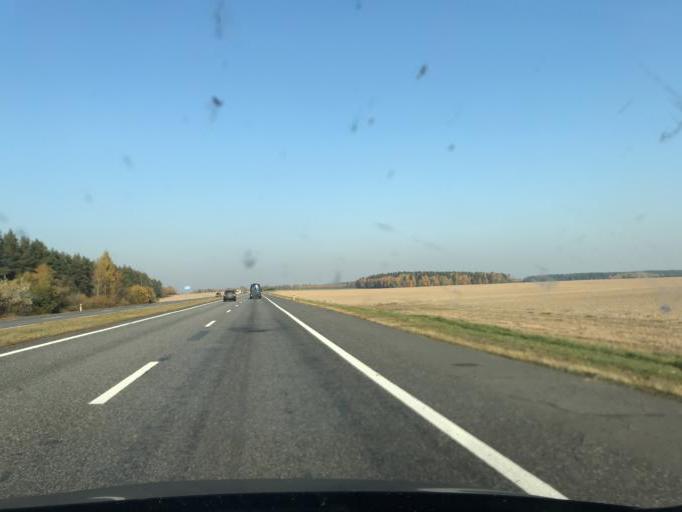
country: BY
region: Minsk
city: Haradzyeya
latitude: 53.3645
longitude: 26.4823
